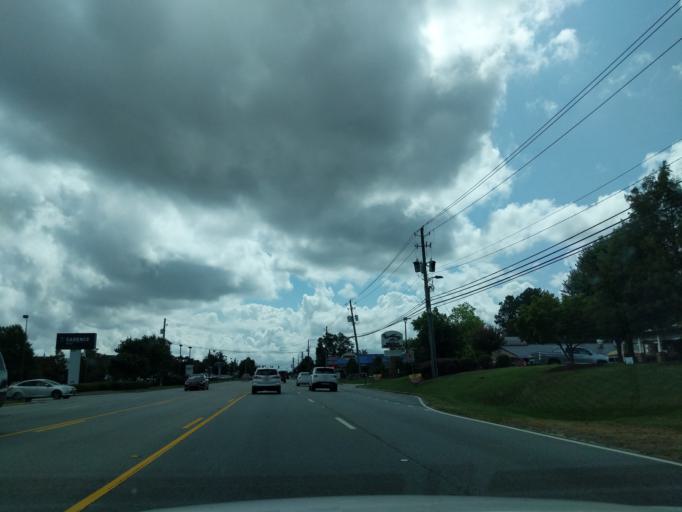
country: US
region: Georgia
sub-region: Columbia County
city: Evans
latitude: 33.5407
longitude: -82.1333
